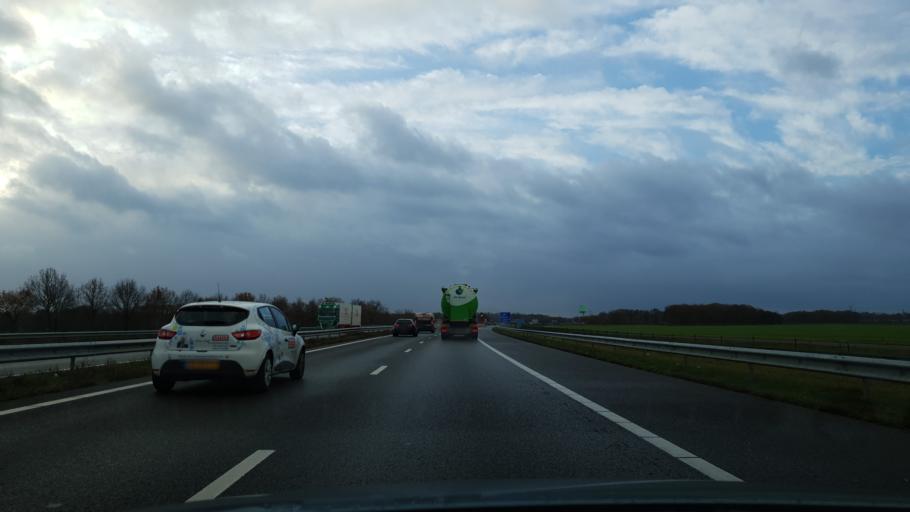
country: NL
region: Limburg
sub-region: Gemeente Venray
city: Venray
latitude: 51.5647
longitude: 5.9940
